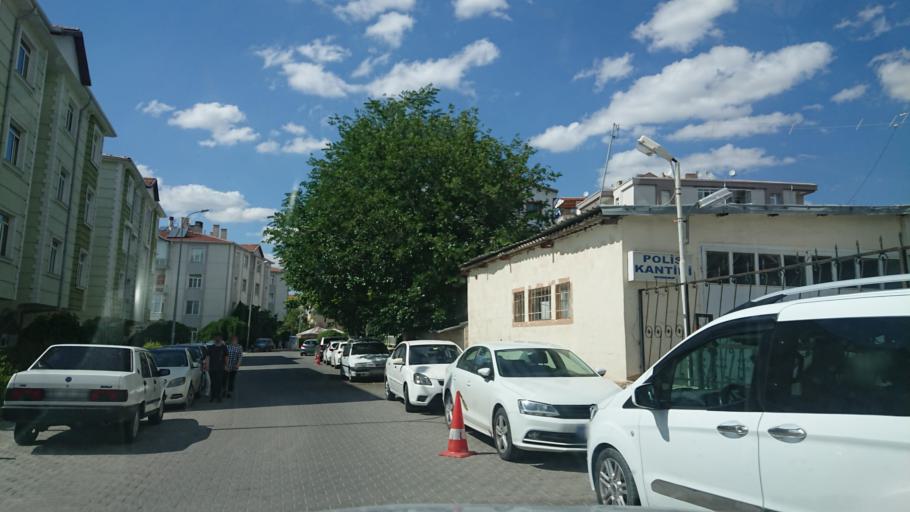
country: TR
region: Kirsehir
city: Kirsehir
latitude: 39.1499
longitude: 34.1588
